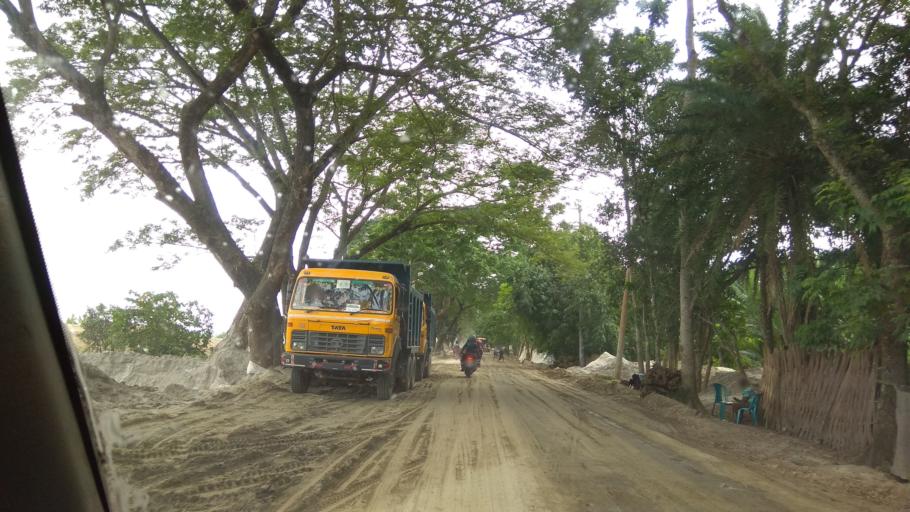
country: BD
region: Khulna
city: Kalia
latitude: 23.1981
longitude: 89.6969
